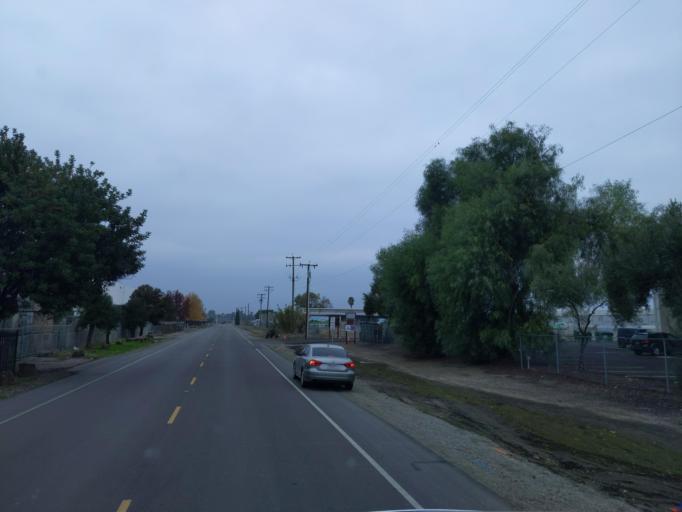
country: US
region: California
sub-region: San Joaquin County
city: August
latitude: 37.9734
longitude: -121.2454
